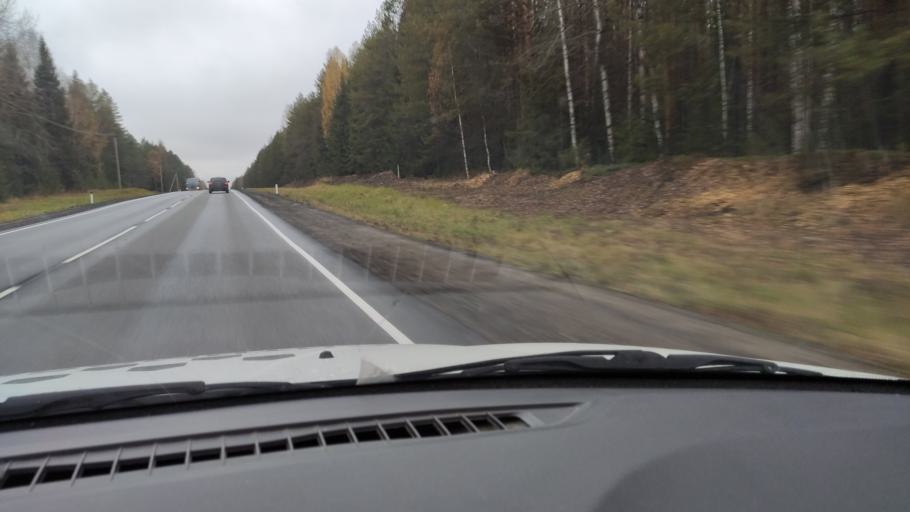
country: RU
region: Kirov
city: Dubrovka
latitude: 58.9143
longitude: 51.1590
